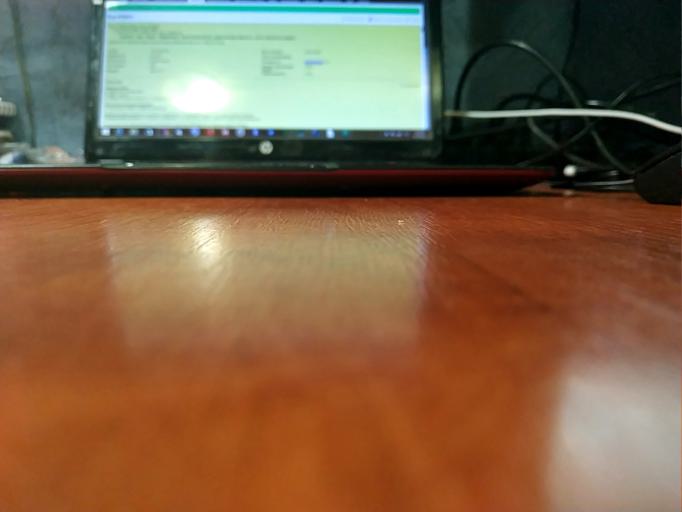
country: RU
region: Vologda
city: Kaduy
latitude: 59.4637
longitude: 37.3299
